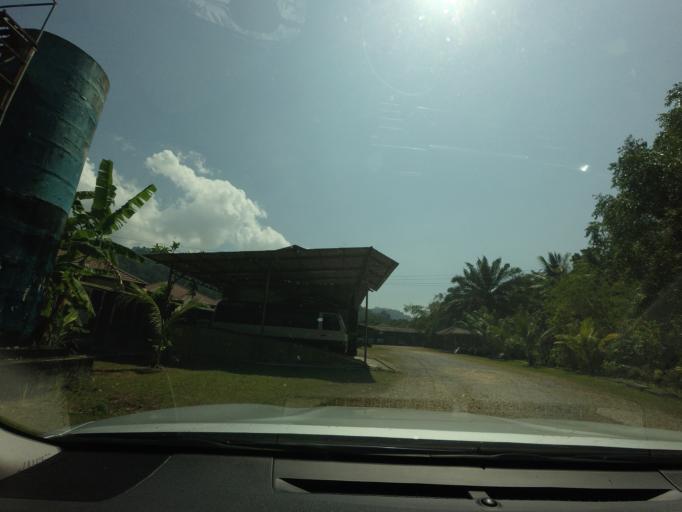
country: TH
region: Phangnga
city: Ban Khao Lak
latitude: 8.6599
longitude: 98.2544
